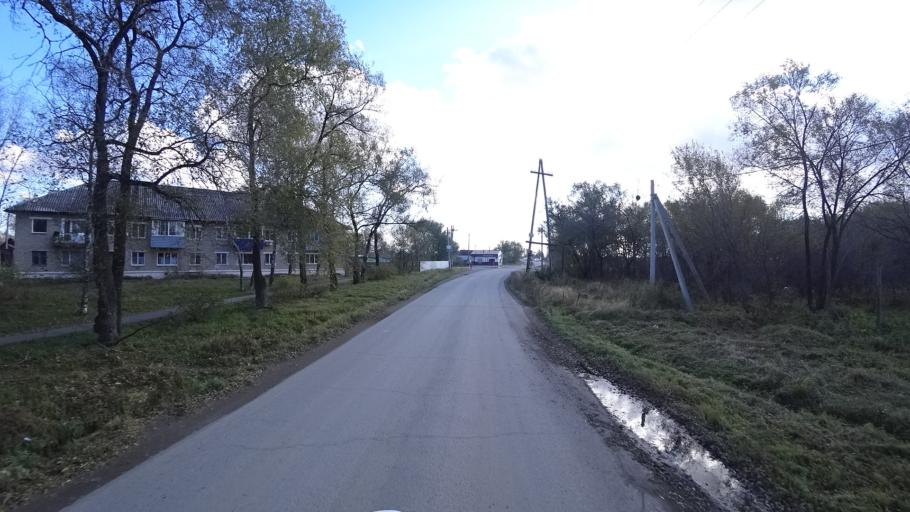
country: RU
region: Khabarovsk Krai
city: Amursk
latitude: 50.0946
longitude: 136.4998
